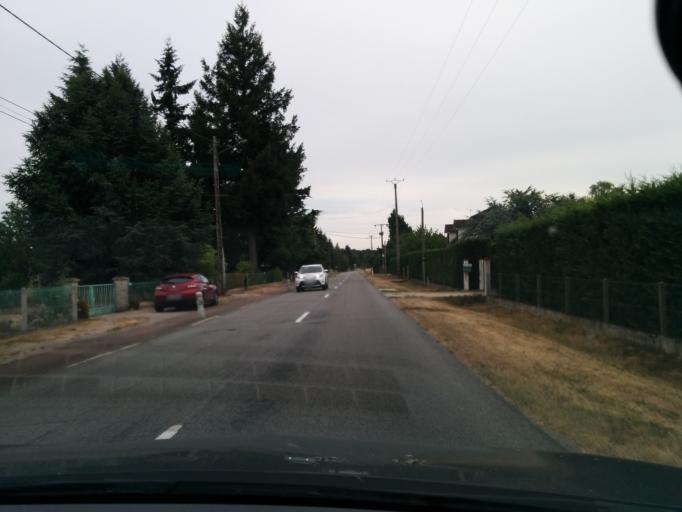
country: FR
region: Centre
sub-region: Departement du Loiret
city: Tigy
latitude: 47.7905
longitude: 2.1986
